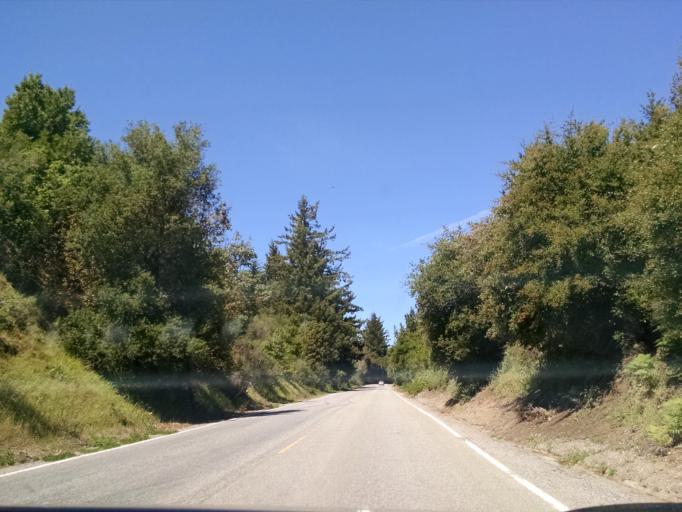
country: US
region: California
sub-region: San Mateo County
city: Portola Valley
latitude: 37.3417
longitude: -122.2215
